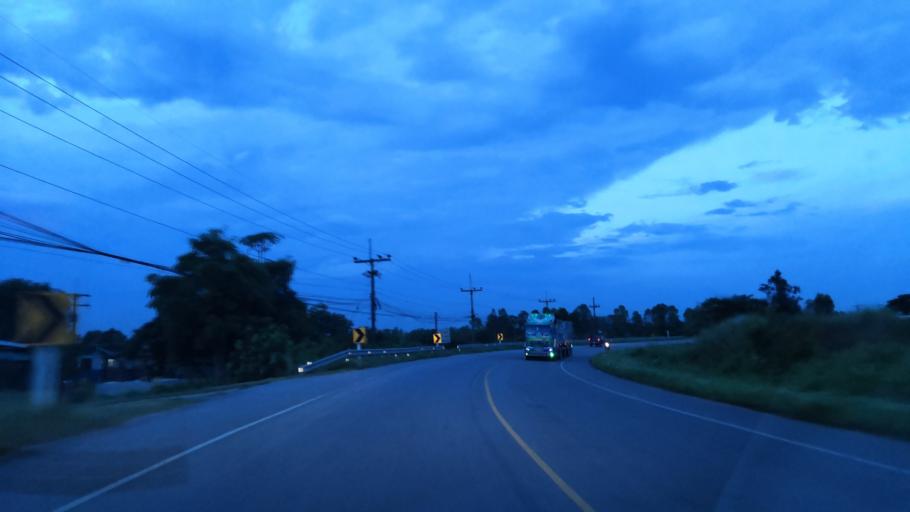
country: TH
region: Chiang Rai
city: Wiang Chiang Rung
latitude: 19.9701
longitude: 100.0128
